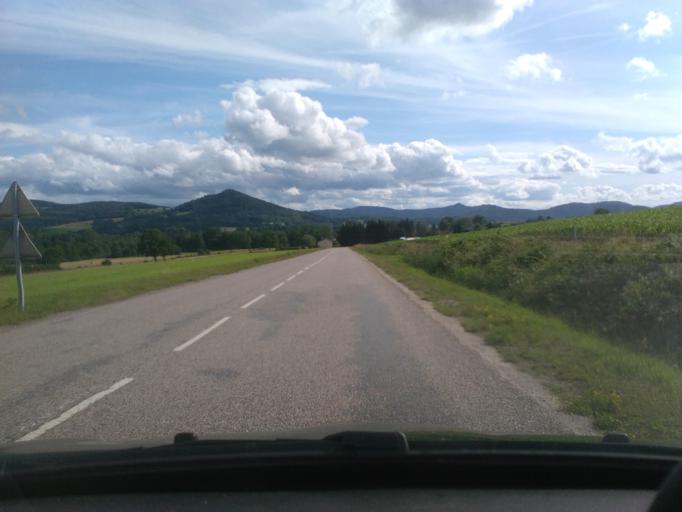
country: FR
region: Lorraine
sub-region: Departement des Vosges
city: Granges-sur-Vologne
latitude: 48.2057
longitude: 6.8018
